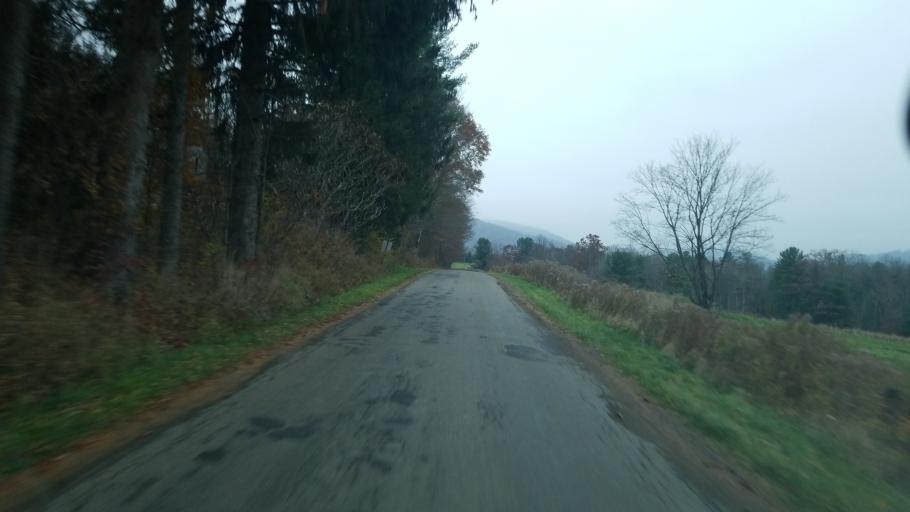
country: US
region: Pennsylvania
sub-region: McKean County
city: Smethport
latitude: 41.7917
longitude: -78.4274
